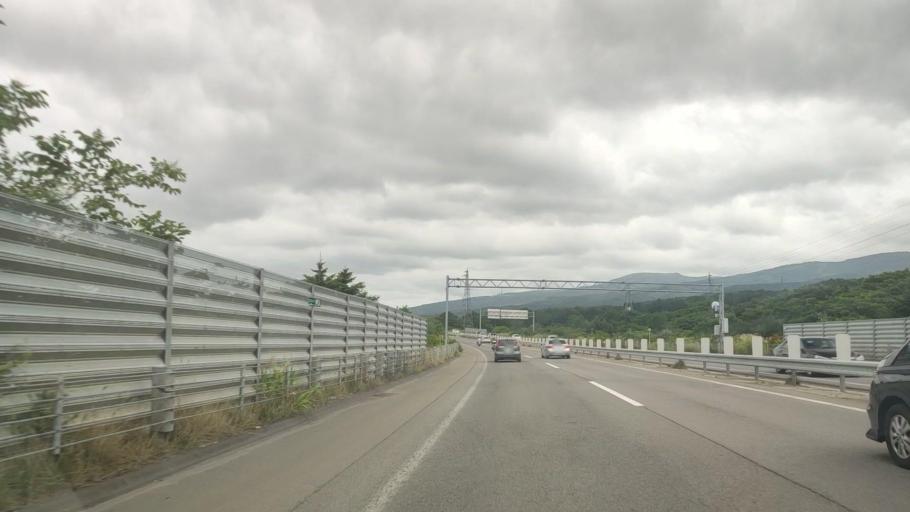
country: JP
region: Hokkaido
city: Nanae
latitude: 41.8551
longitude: 140.7383
